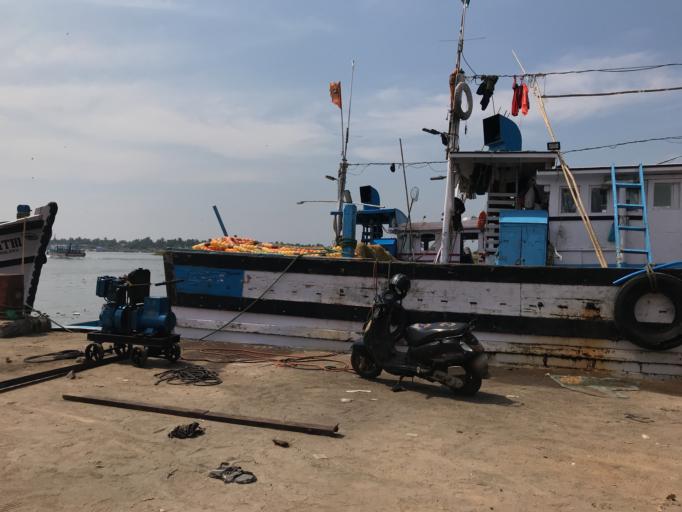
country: IN
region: Karnataka
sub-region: Dakshina Kannada
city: Ullal
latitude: 12.8588
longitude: 74.8324
